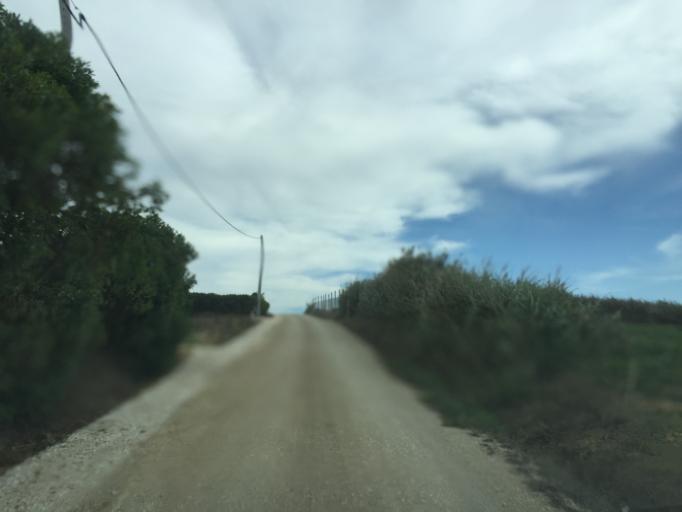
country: PT
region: Lisbon
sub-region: Lourinha
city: Lourinha
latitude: 39.1968
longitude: -9.3437
